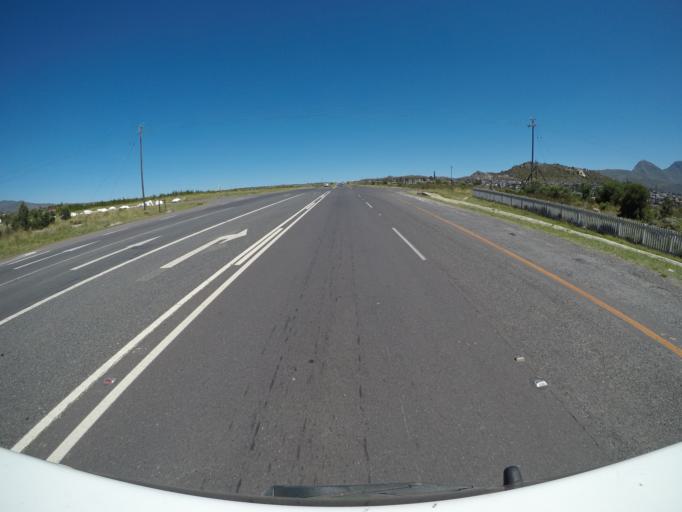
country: ZA
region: Western Cape
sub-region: Overberg District Municipality
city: Grabouw
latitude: -34.1624
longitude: 18.9853
